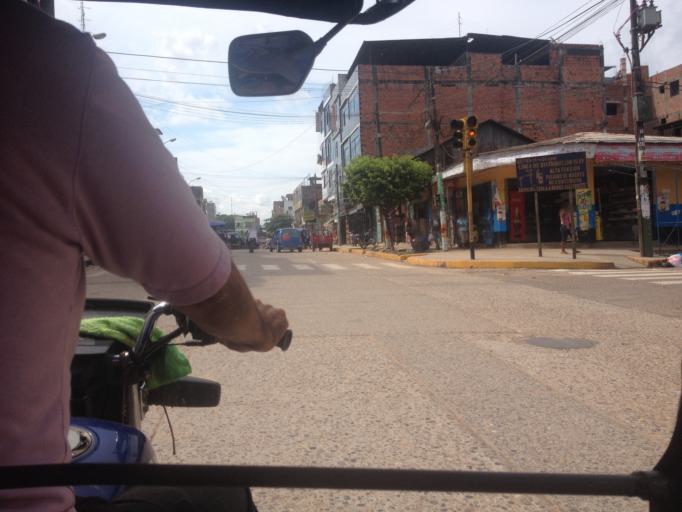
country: PE
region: Ucayali
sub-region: Provincia de Coronel Portillo
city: Pucallpa
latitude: -8.3837
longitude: -74.5343
